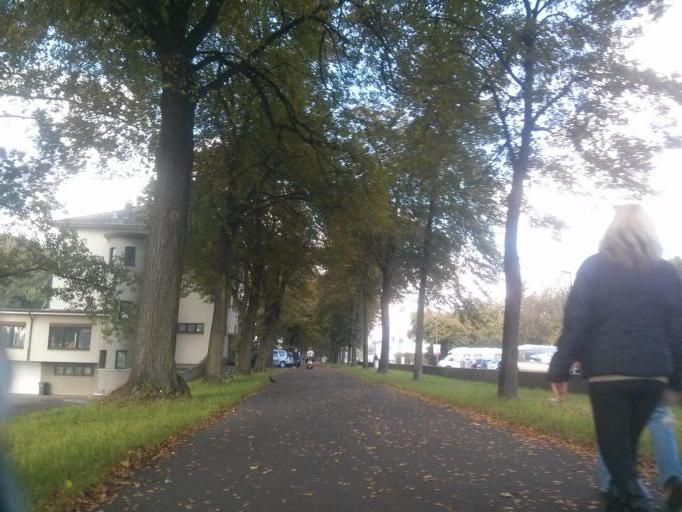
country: DE
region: North Rhine-Westphalia
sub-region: Regierungsbezirk Koln
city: Poll
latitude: 50.9123
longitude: 6.9839
